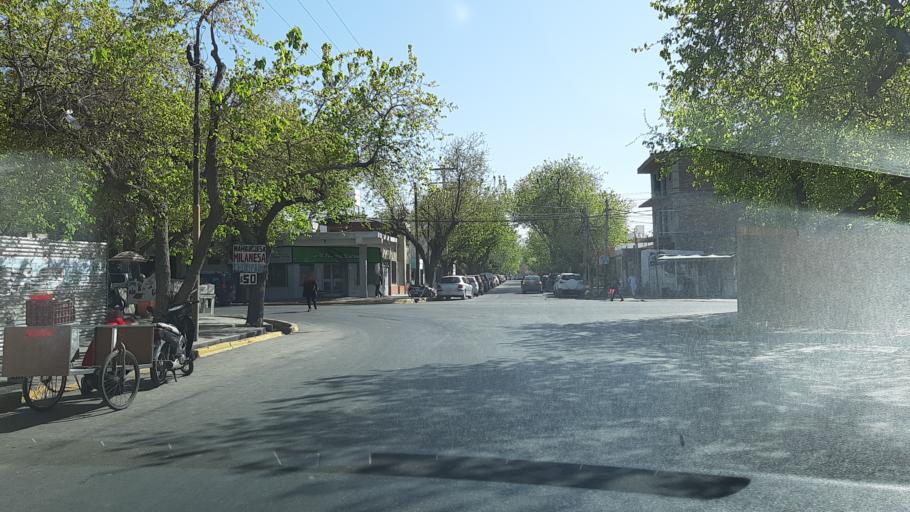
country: AR
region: San Juan
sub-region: Departamento de Santa Lucia
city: Santa Lucia
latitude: -31.5385
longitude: -68.5117
